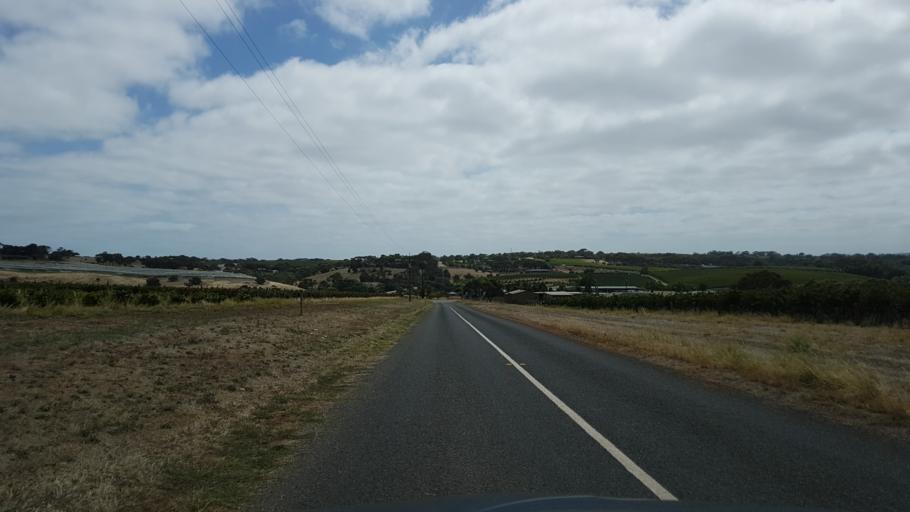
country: AU
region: South Australia
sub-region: Onkaparinga
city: McLaren Vale
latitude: -35.2129
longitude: 138.5175
